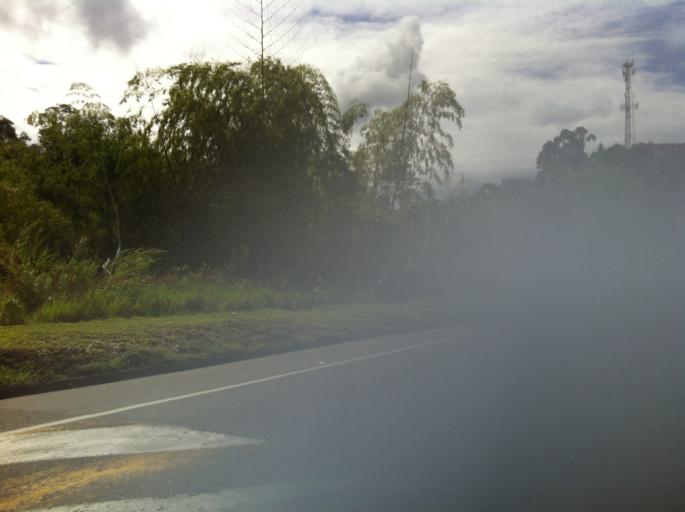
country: CO
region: Quindio
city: Circasia
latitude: 4.5842
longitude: -75.6392
